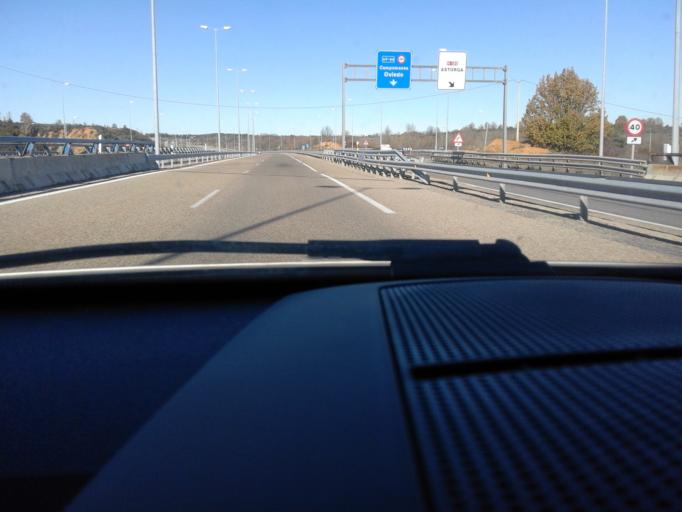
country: ES
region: Castille and Leon
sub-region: Provincia de Leon
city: Valverde de la Virgen
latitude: 42.5740
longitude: -5.6619
